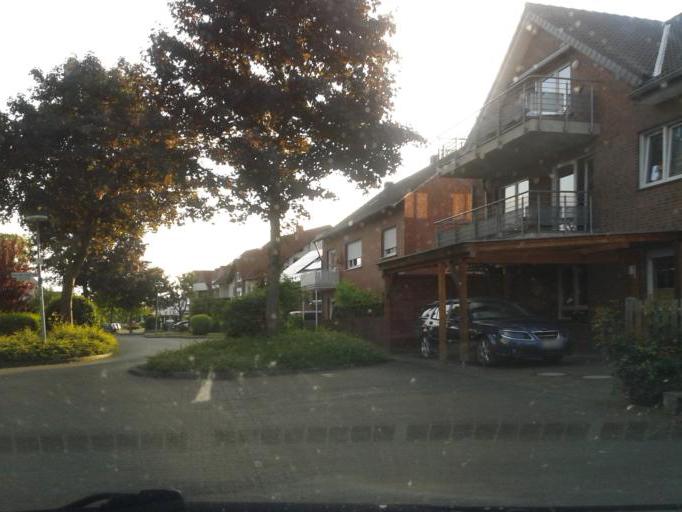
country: DE
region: North Rhine-Westphalia
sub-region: Regierungsbezirk Detmold
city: Paderborn
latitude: 51.7429
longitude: 8.6922
